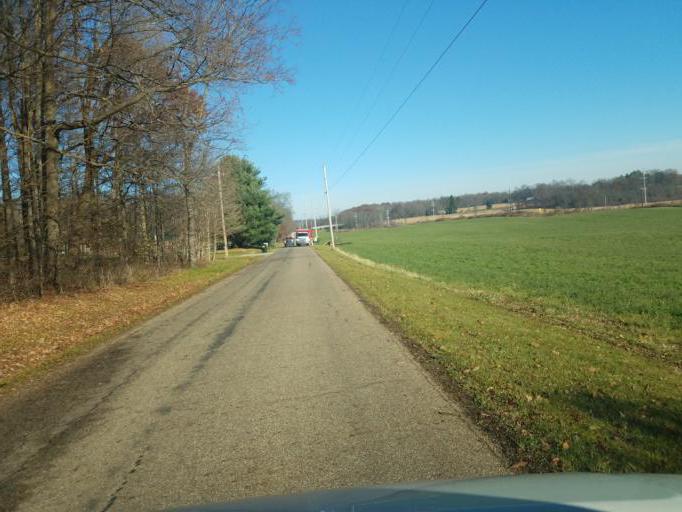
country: US
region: Ohio
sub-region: Richland County
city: Lincoln Heights
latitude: 40.7184
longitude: -82.4463
